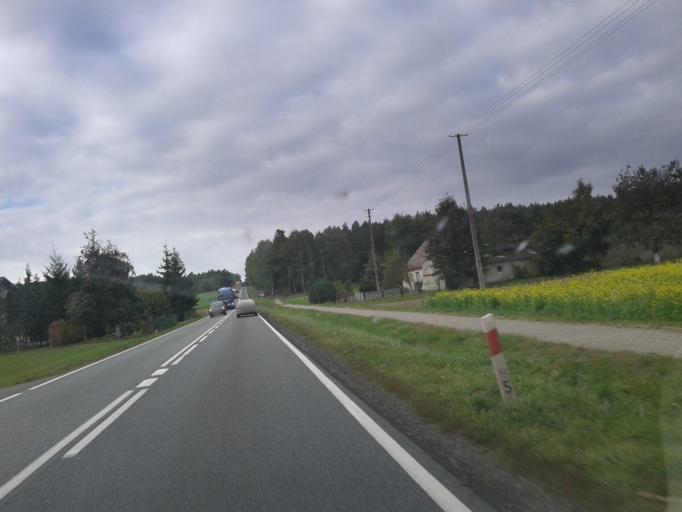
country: PL
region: Kujawsko-Pomorskie
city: Kamien Krajenski
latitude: 53.5422
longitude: 17.5161
